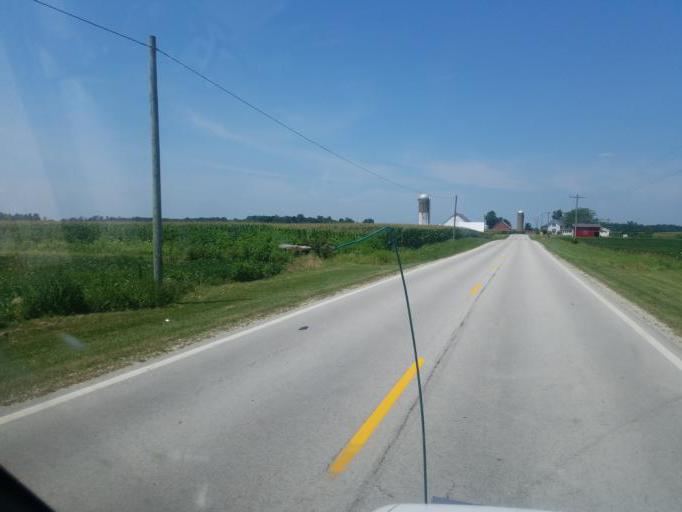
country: US
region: Ohio
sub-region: Shelby County
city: Fort Loramie
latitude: 40.3506
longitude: -84.4346
